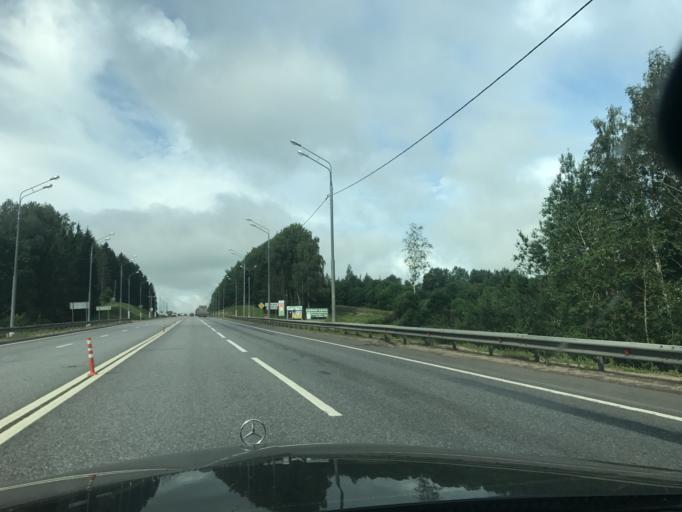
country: RU
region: Smolensk
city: Kardymovo
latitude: 55.0223
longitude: 32.3181
